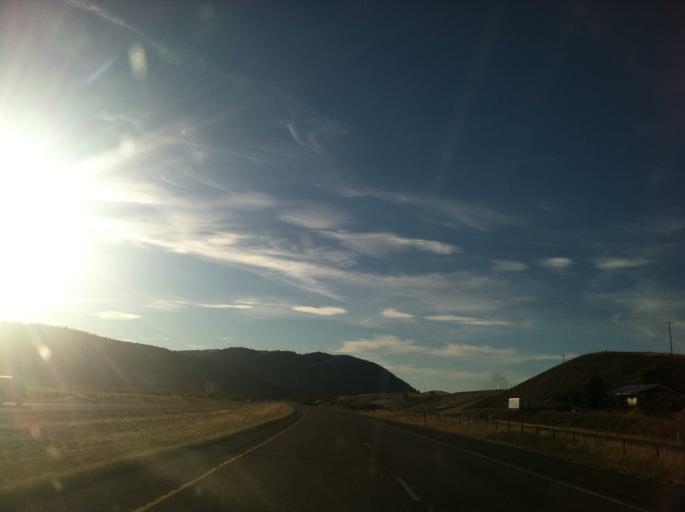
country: US
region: Montana
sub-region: Granite County
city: Philipsburg
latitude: 46.6777
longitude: -113.1744
